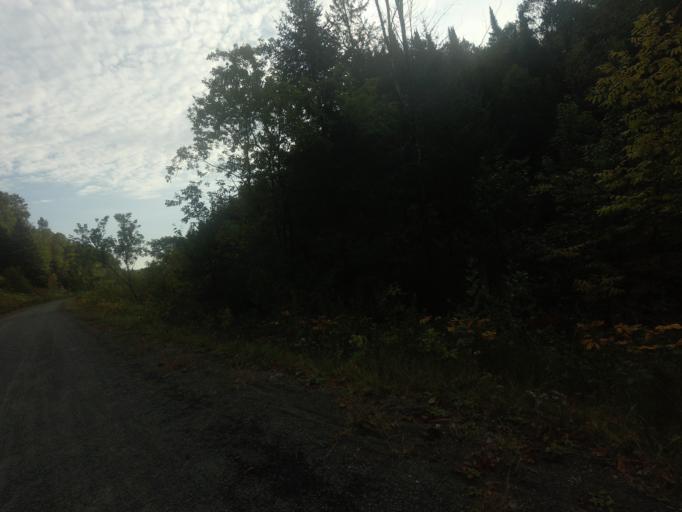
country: CA
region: Quebec
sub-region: Laurentides
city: Sainte-Adele
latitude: 45.9277
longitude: -74.1311
